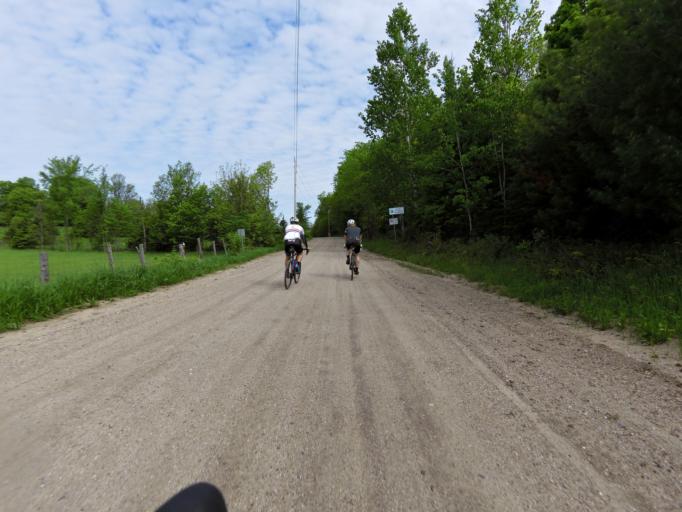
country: CA
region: Quebec
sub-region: Outaouais
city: Wakefield
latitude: 45.7697
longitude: -75.9192
